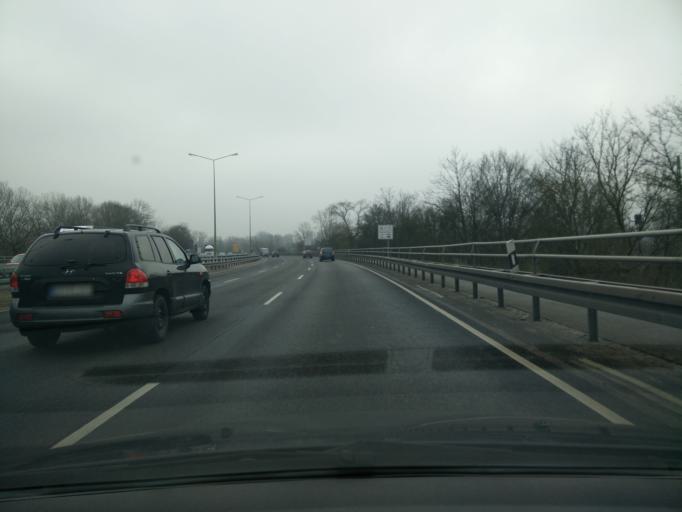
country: DE
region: Rheinland-Pfalz
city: Worth am Rhein
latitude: 49.0365
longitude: 8.3057
